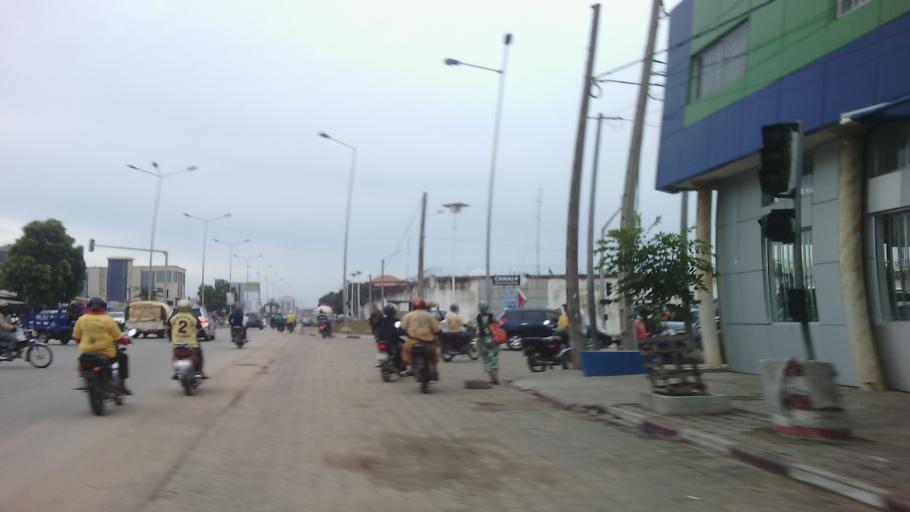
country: BJ
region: Littoral
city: Cotonou
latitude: 6.3635
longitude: 2.4189
